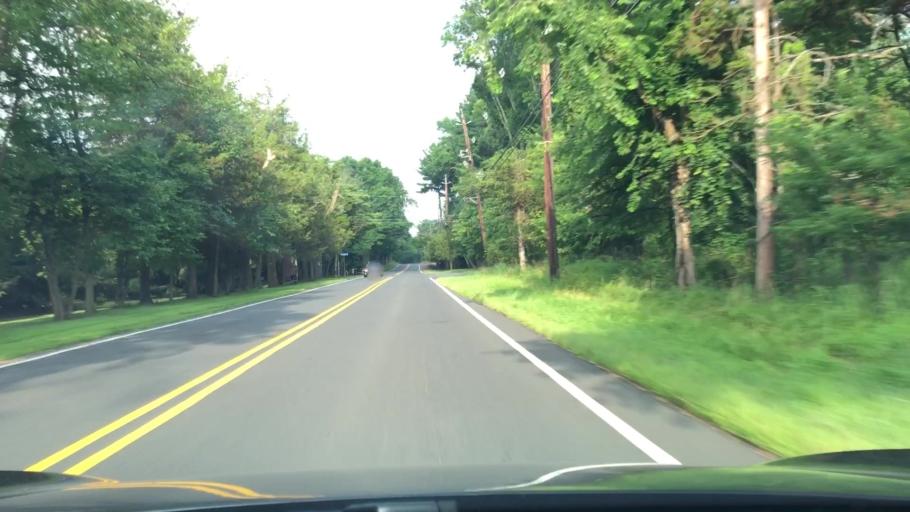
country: US
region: New Jersey
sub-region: Mercer County
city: Pennington
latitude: 40.3397
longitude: -74.7493
